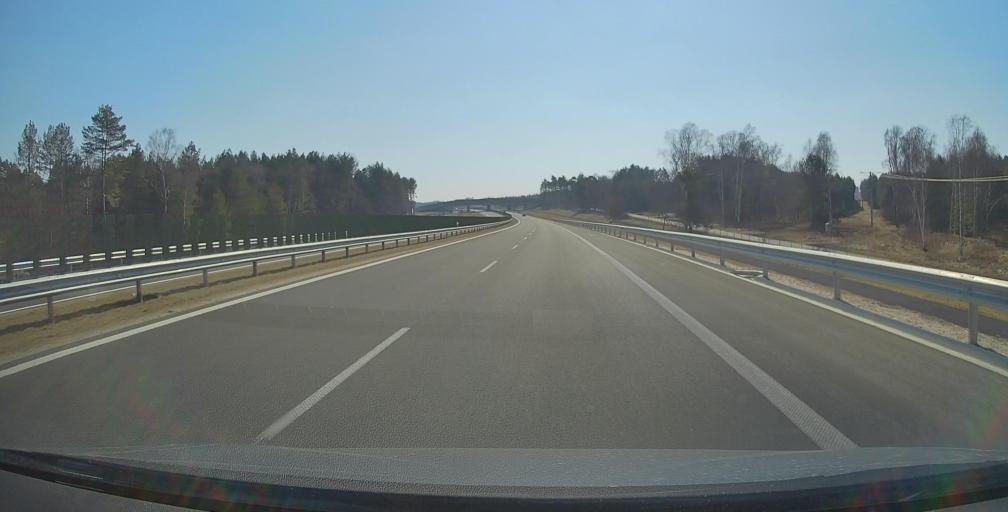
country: PL
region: Subcarpathian Voivodeship
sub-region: Powiat nizanski
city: Konczyce
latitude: 50.4022
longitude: 22.1376
